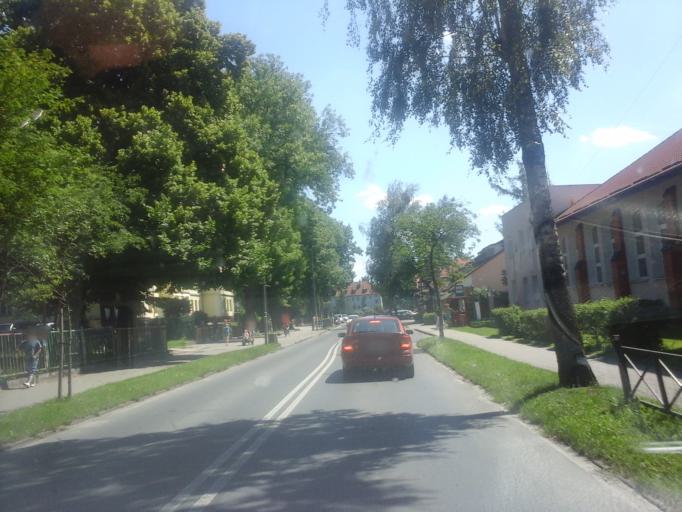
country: PL
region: West Pomeranian Voivodeship
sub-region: Powiat bialogardzki
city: Bialogard
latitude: 54.0073
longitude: 15.9931
